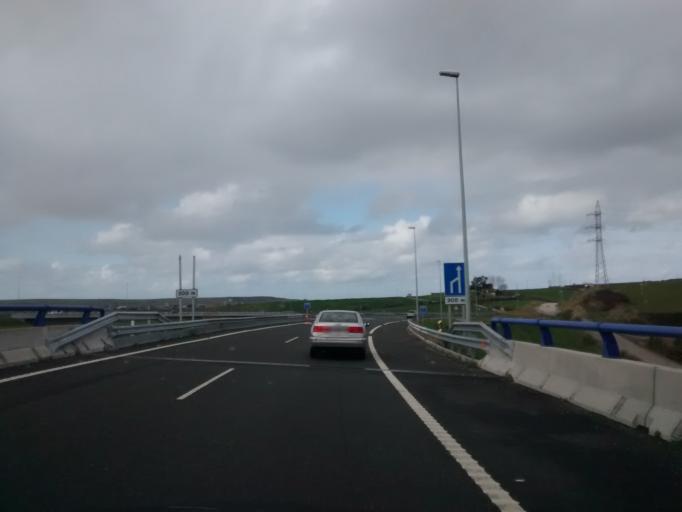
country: ES
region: Cantabria
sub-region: Provincia de Cantabria
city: Santa Cruz de Bezana
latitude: 43.4469
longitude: -3.8804
